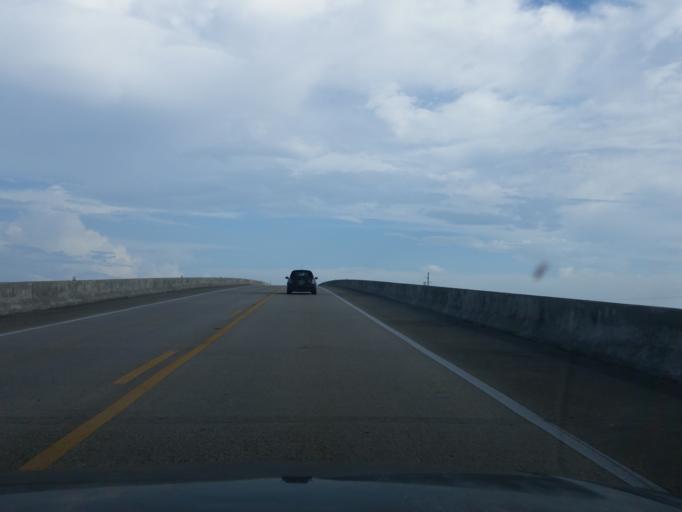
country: US
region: Alabama
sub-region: Mobile County
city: Dauphin Island
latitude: 30.2919
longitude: -88.1301
